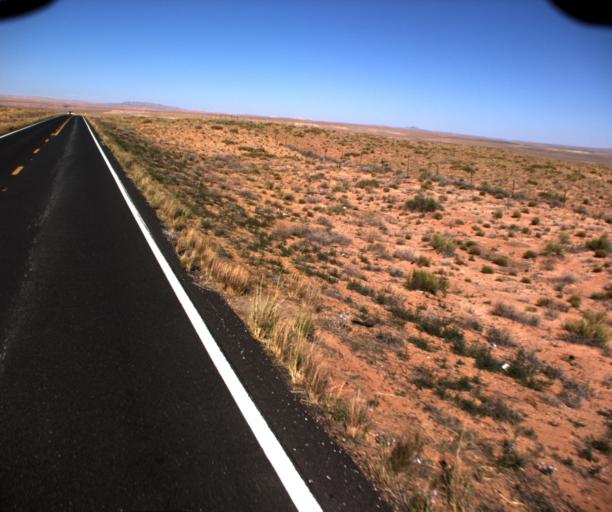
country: US
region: Arizona
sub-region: Coconino County
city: Tuba City
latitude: 36.0733
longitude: -111.1847
